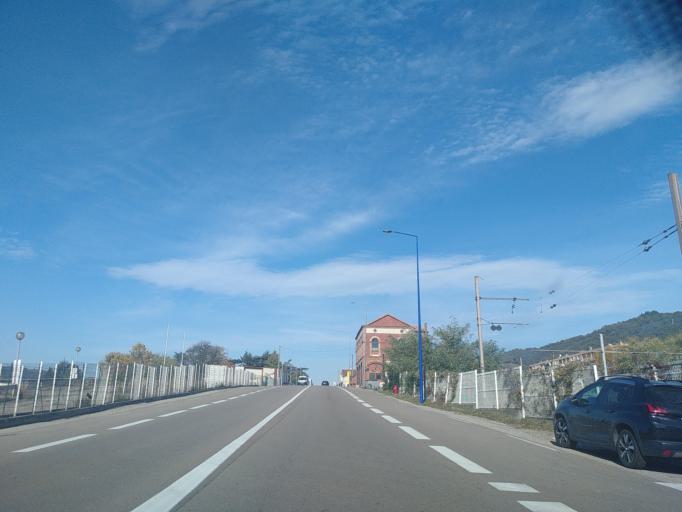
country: FR
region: Rhone-Alpes
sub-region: Departement de la Drome
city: Saint-Vallier
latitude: 45.1883
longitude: 4.8141
